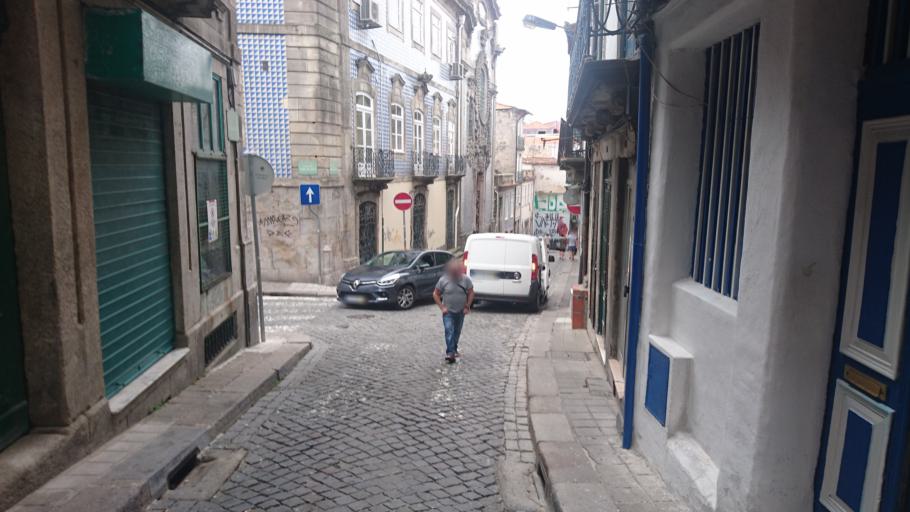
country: PT
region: Porto
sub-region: Porto
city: Porto
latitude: 41.1449
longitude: -8.6080
